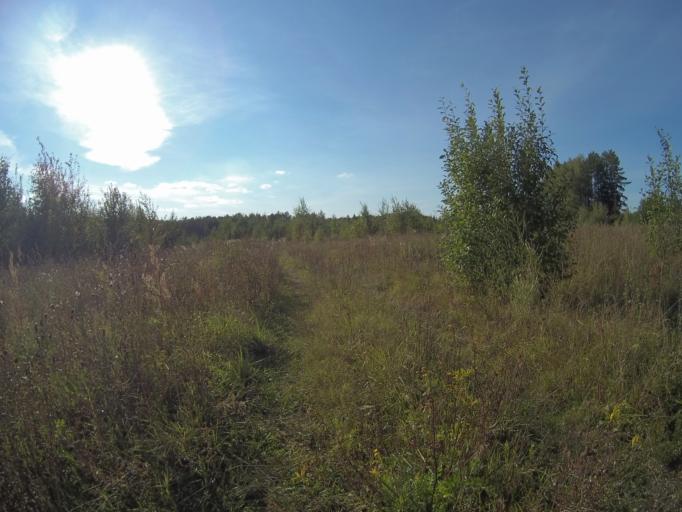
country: RU
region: Vladimir
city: Kommunar
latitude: 56.0620
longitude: 40.5071
